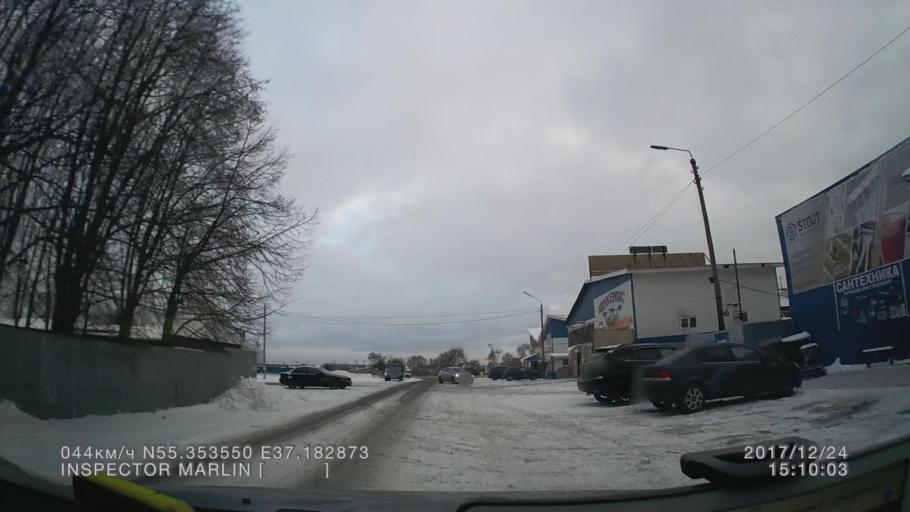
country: RU
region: Moskovskaya
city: Troitsk
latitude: 55.3535
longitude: 37.1830
